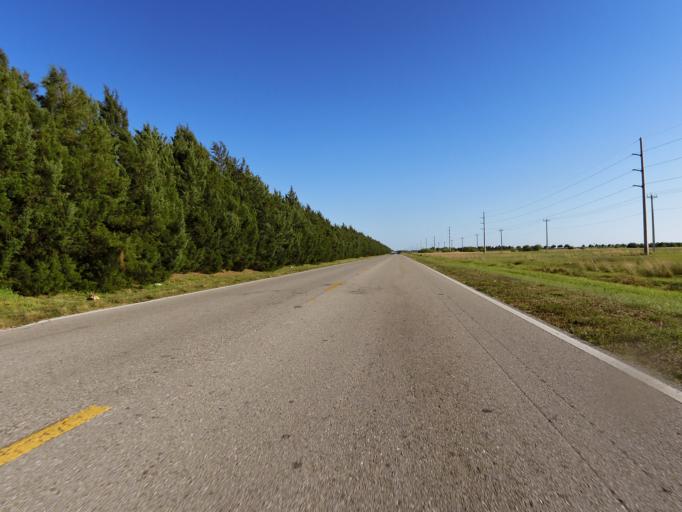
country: US
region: Florida
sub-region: Collier County
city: Immokalee
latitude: 26.3471
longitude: -81.4168
